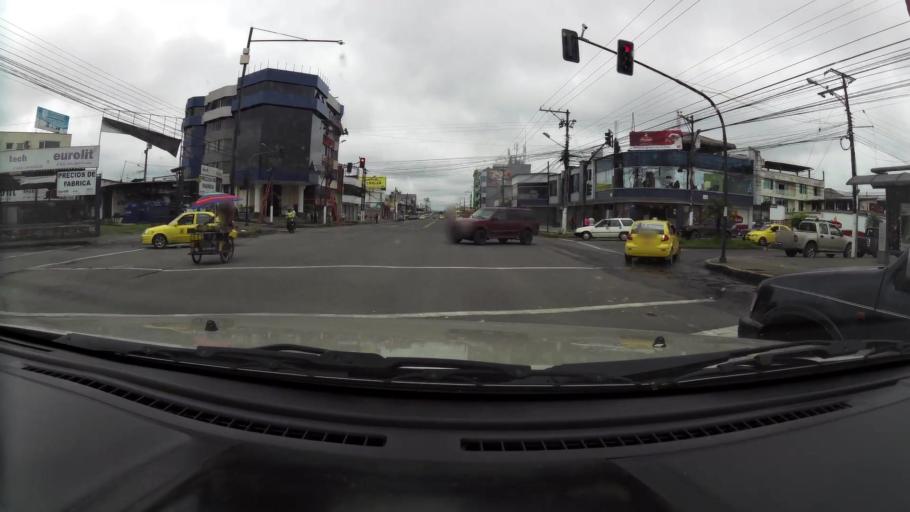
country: EC
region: Santo Domingo de los Tsachilas
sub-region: Canton Santo Domingo de los Colorados
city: Santo Domingo de los Colorados
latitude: -0.2453
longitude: -79.1683
